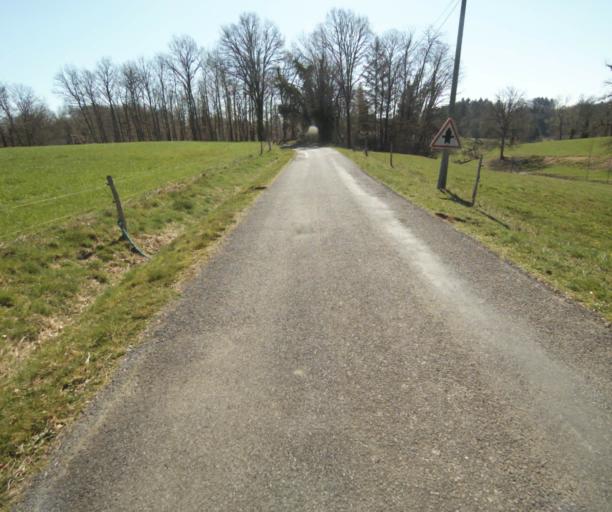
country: FR
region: Limousin
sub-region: Departement de la Correze
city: Saint-Mexant
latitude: 45.3094
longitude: 1.6458
